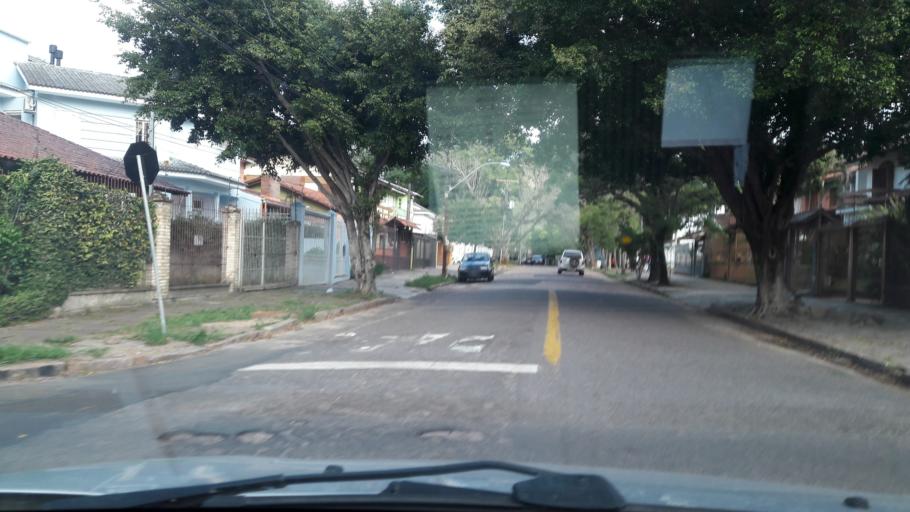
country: BR
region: Rio Grande do Sul
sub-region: Porto Alegre
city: Porto Alegre
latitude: -30.0833
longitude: -51.2074
